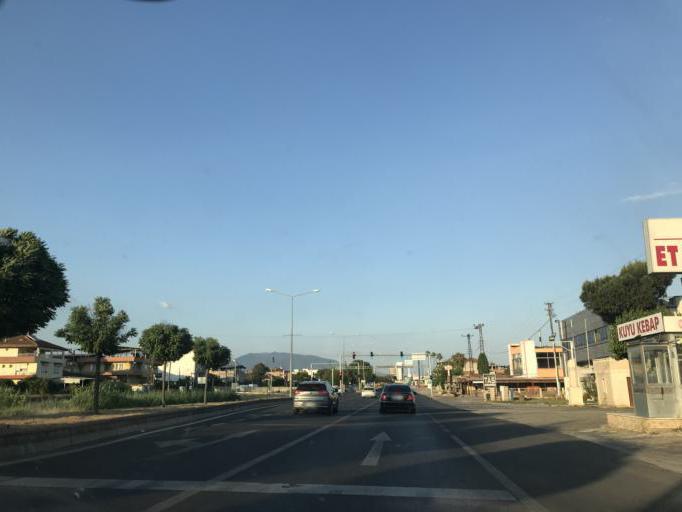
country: TR
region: Aydin
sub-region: Nazilli
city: Isabeyli
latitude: 37.9006
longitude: 28.2858
